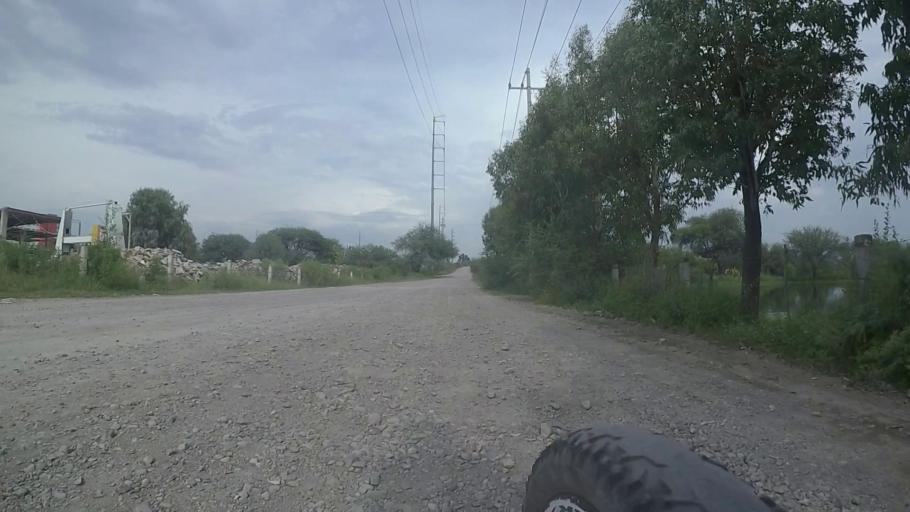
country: MX
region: Aguascalientes
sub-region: Aguascalientes
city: Penuelas (El Cienegal)
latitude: 21.7264
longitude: -102.2802
